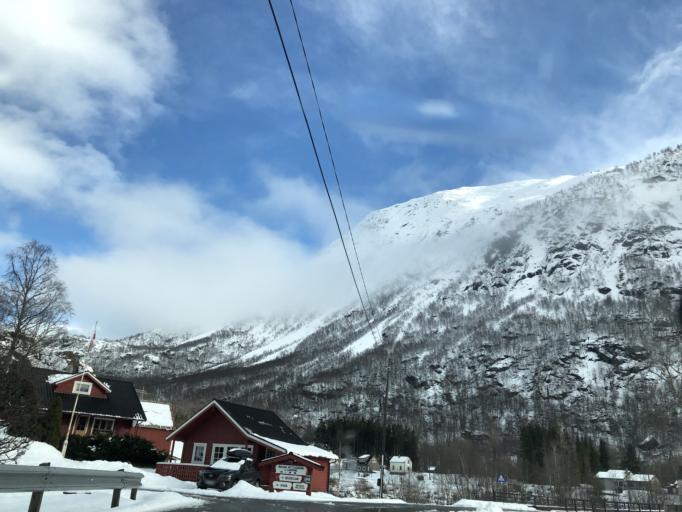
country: NO
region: Hordaland
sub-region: Odda
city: Odda
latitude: 59.8307
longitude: 6.8271
